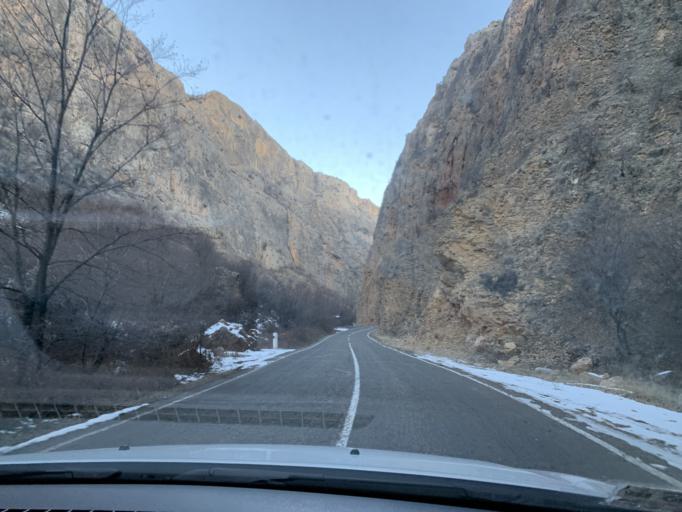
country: AM
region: Vayots' Dzori Marz
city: Areni
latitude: 39.7168
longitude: 45.2063
